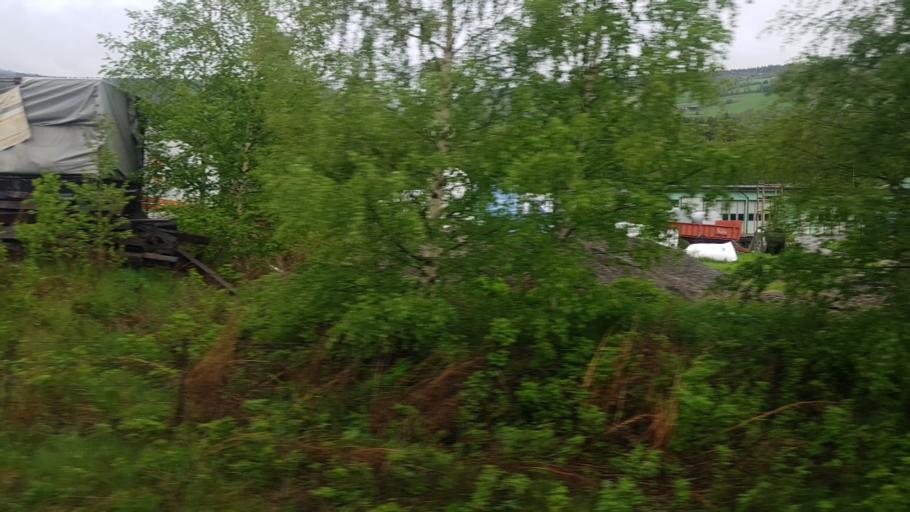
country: NO
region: Oppland
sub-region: Sor-Fron
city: Hundorp
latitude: 61.5630
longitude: 9.9255
